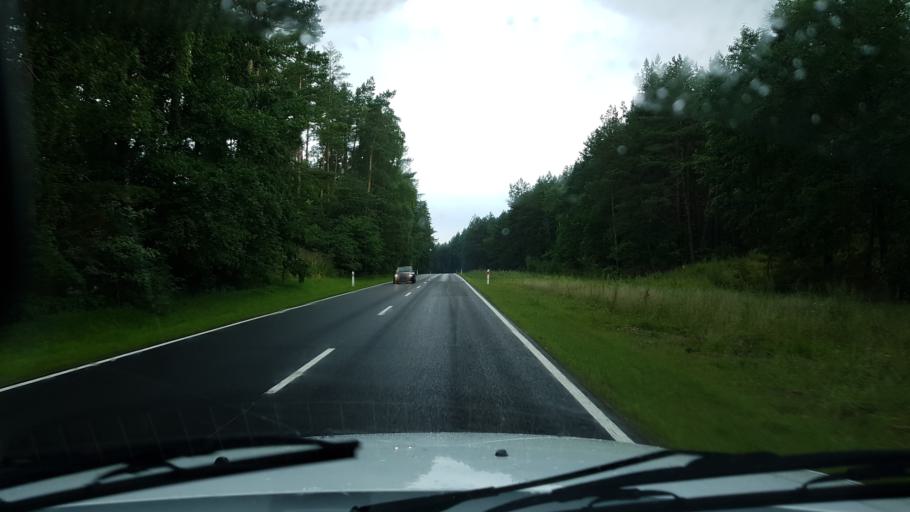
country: PL
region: West Pomeranian Voivodeship
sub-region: Powiat goleniowski
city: Mosty
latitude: 53.4392
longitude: 14.9416
